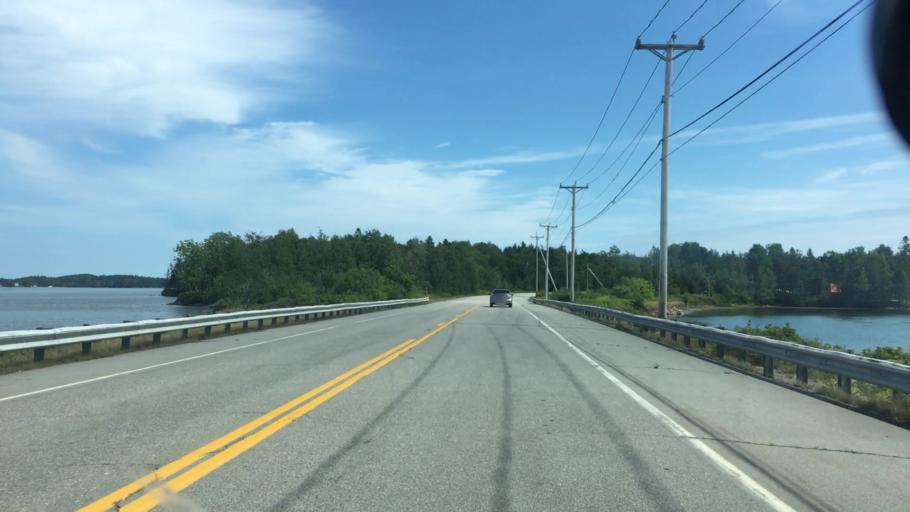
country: US
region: Maine
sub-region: Washington County
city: Eastport
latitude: 44.9387
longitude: -67.0317
